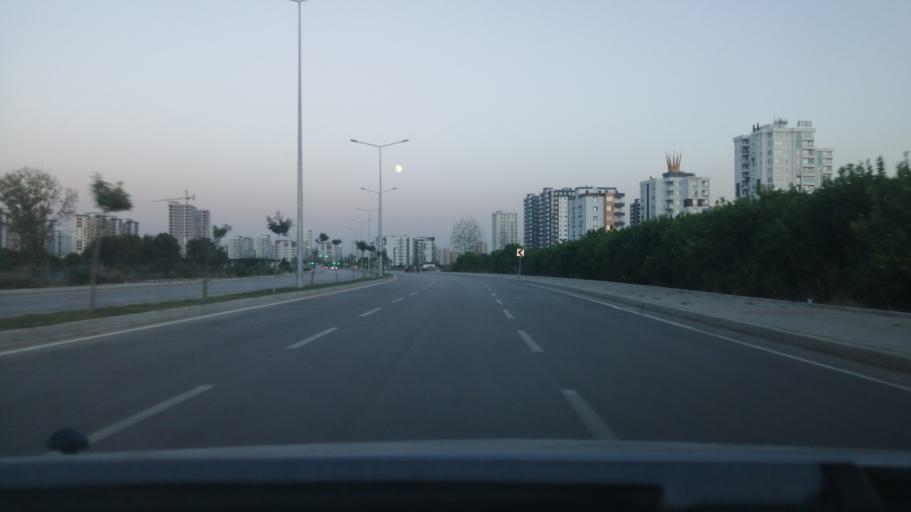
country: TR
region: Adana
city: Seyhan
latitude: 37.0153
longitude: 35.2527
